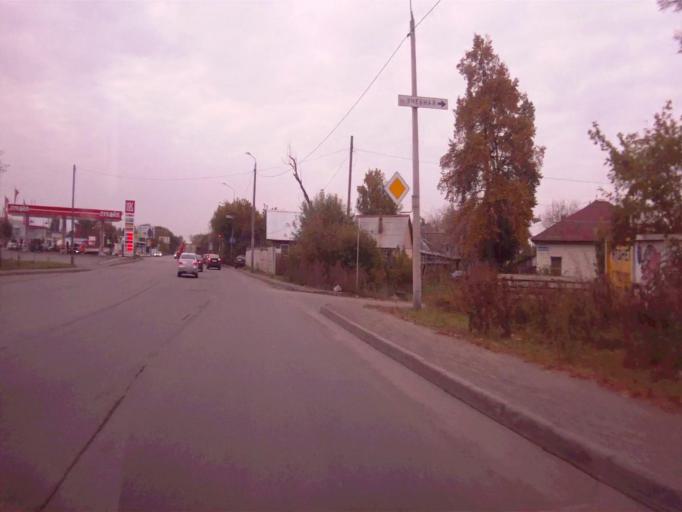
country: RU
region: Chelyabinsk
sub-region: Gorod Chelyabinsk
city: Chelyabinsk
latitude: 55.1327
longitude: 61.3850
